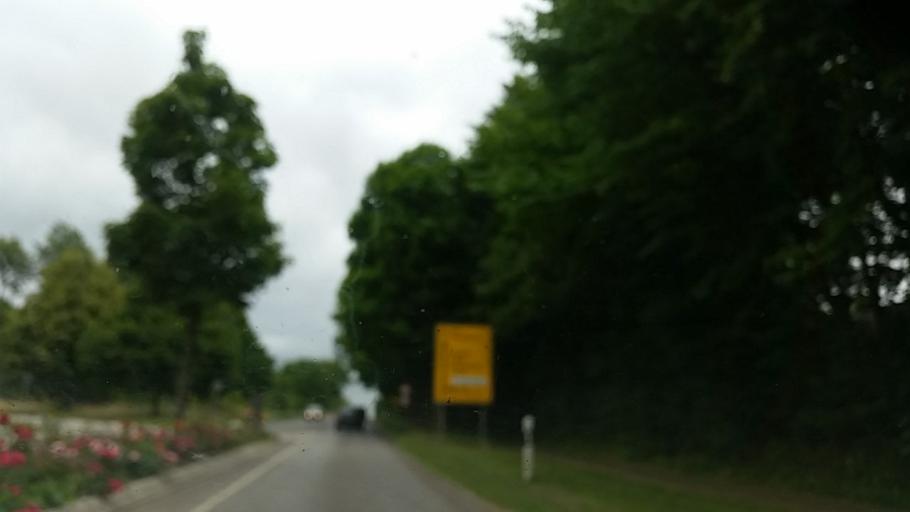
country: DE
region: Schleswig-Holstein
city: Windeby
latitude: 54.4841
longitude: 9.8116
